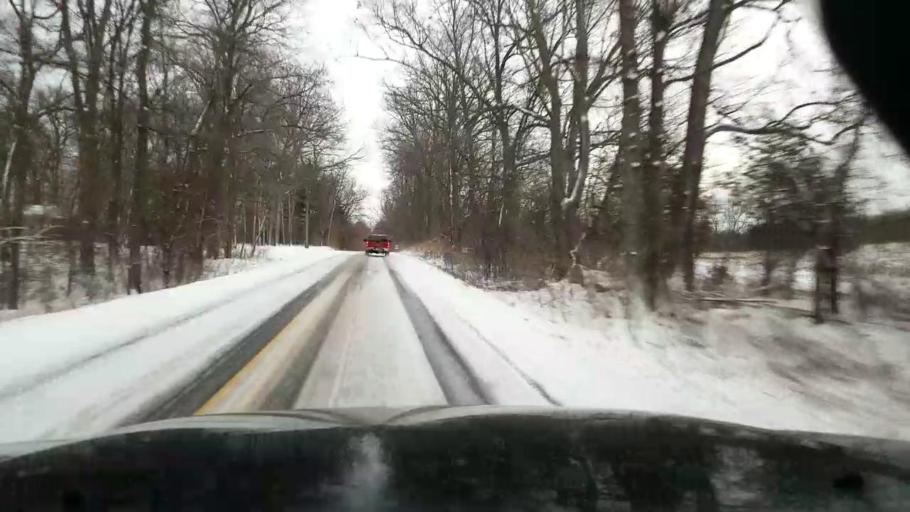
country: US
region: Michigan
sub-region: Jackson County
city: Spring Arbor
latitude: 42.1399
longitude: -84.4988
